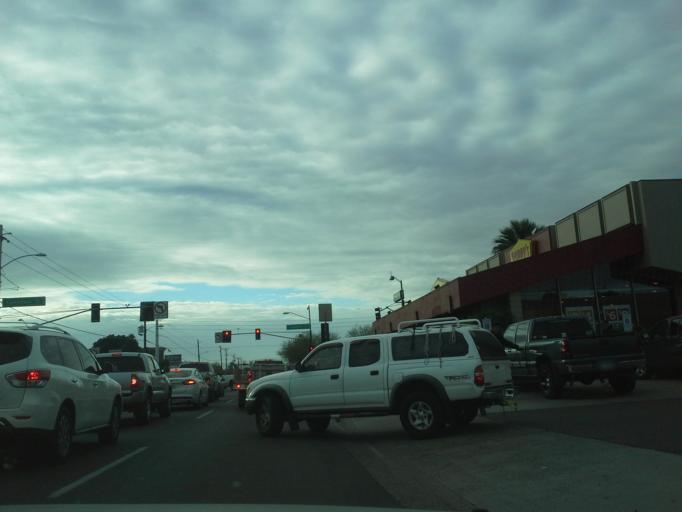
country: US
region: Arizona
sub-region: Maricopa County
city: Phoenix
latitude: 33.5098
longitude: -112.0651
